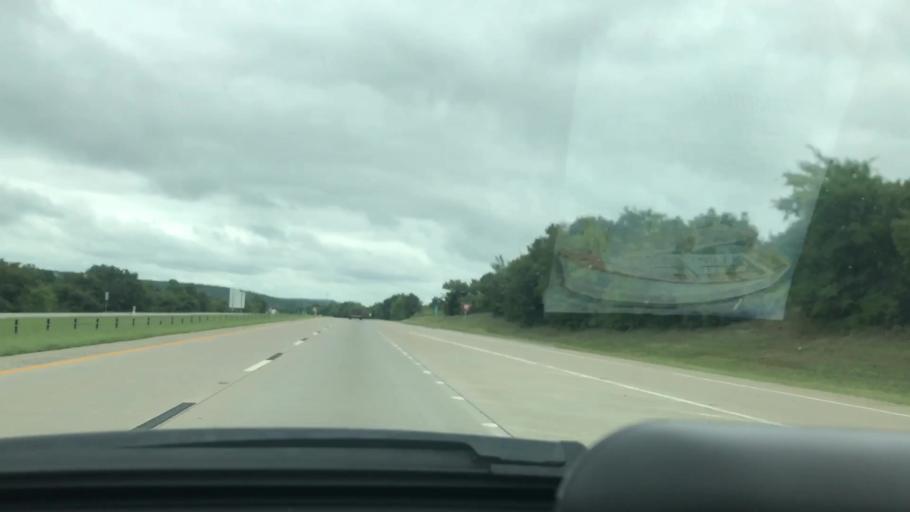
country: US
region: Oklahoma
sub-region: Pittsburg County
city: Krebs
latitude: 35.0034
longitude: -95.7194
